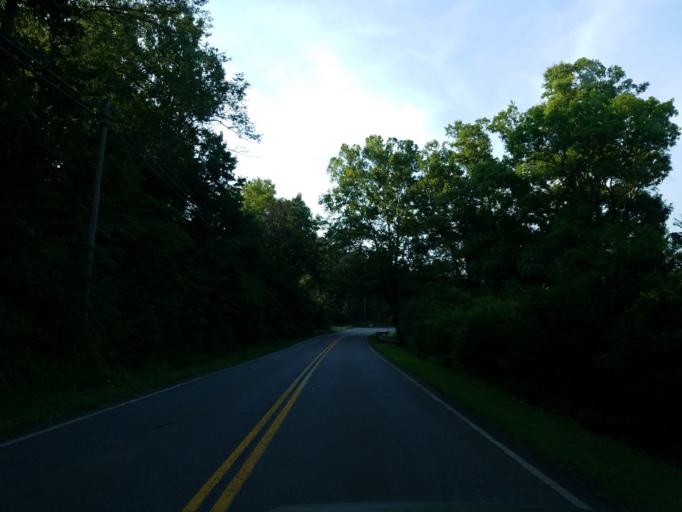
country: US
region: Georgia
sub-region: Gilmer County
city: Ellijay
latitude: 34.5788
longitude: -84.5363
